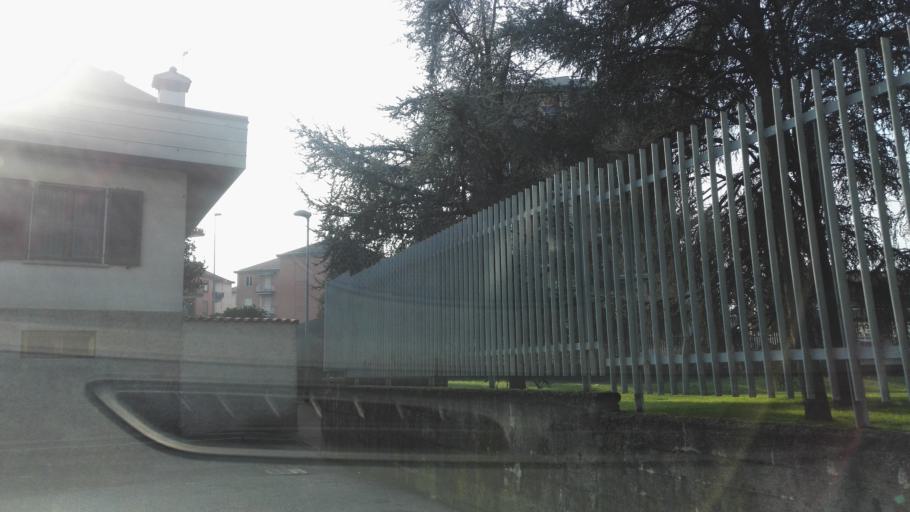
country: IT
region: Lombardy
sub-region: Citta metropolitana di Milano
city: San Giuliano Milanese
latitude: 45.3980
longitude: 9.2874
